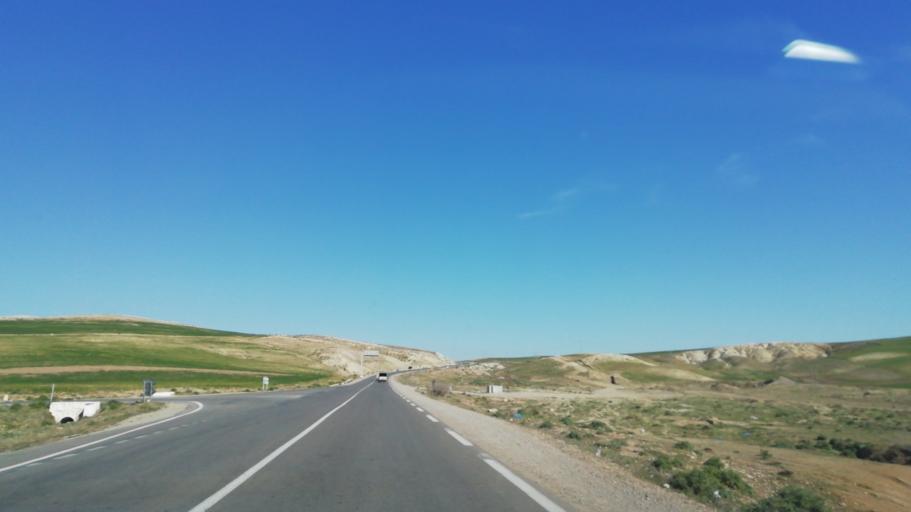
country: DZ
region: Mascara
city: Oued el Abtal
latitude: 35.4488
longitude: 0.6212
